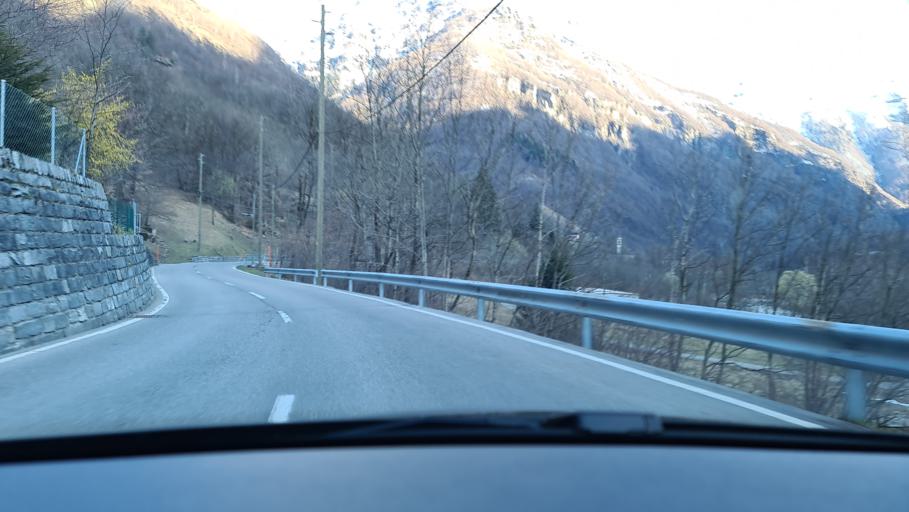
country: CH
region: Ticino
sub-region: Locarno District
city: Lavertezzo
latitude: 46.3452
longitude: 8.7961
